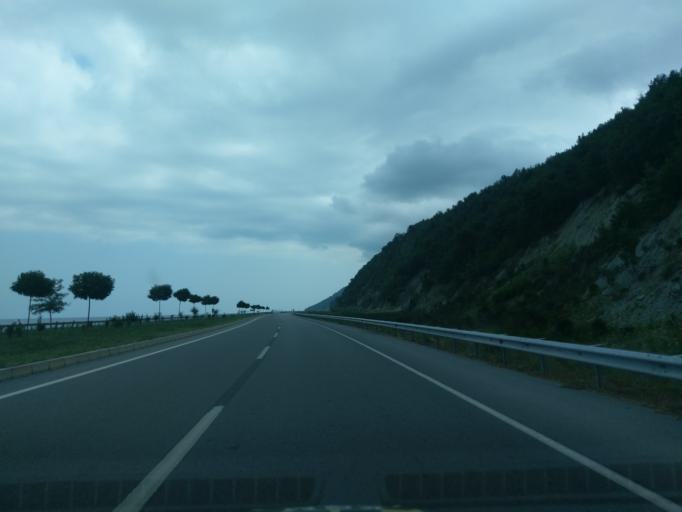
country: TR
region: Sinop
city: Dikmen
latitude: 41.7088
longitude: 35.2971
